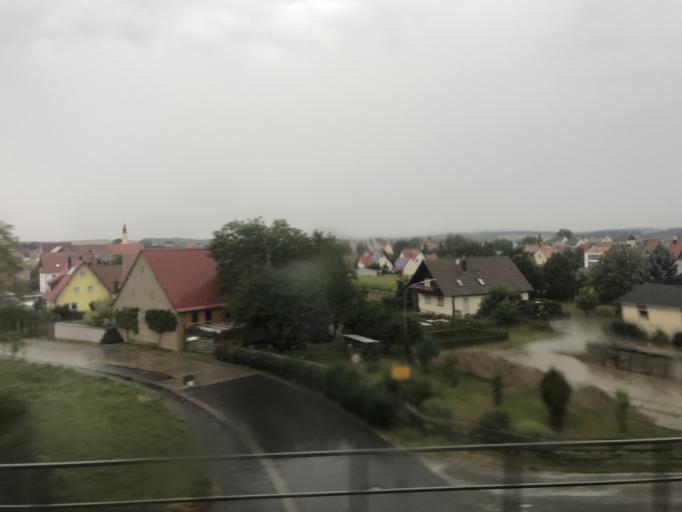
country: DE
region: Bavaria
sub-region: Regierungsbezirk Unterfranken
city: Werneck
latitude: 49.9442
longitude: 10.0856
